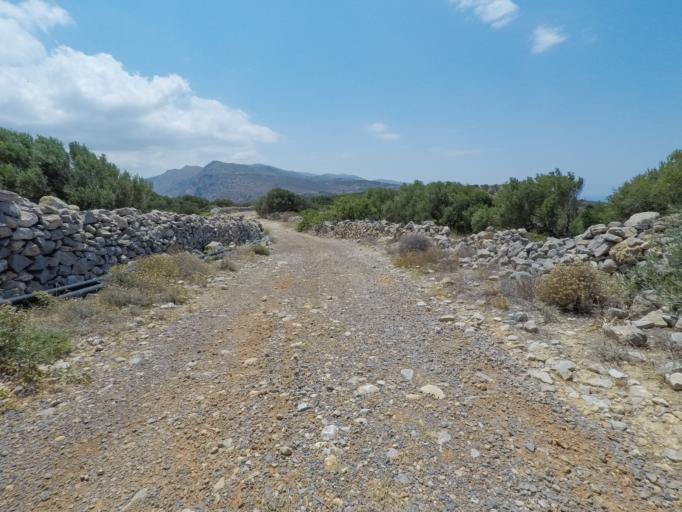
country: GR
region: Crete
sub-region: Nomos Lasithiou
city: Elounda
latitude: 35.3157
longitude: 25.7441
